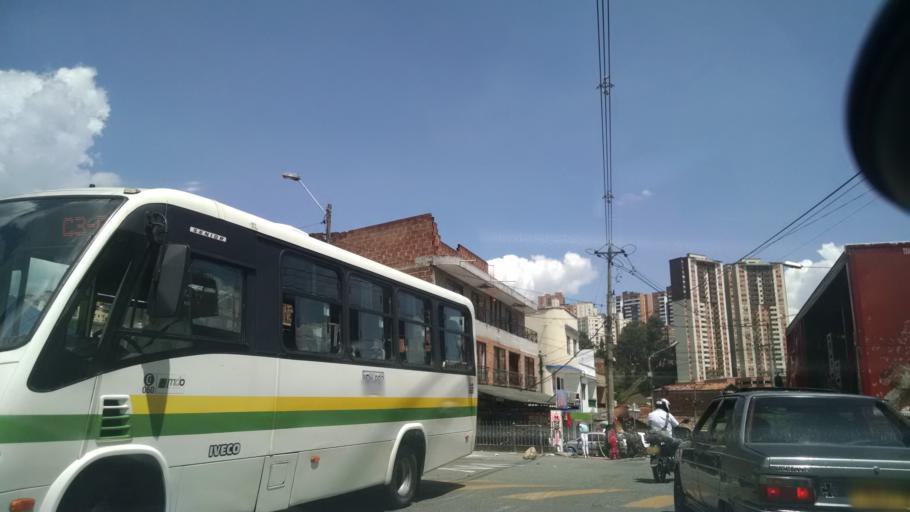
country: CO
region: Antioquia
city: Itagui
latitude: 6.2126
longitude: -75.6027
